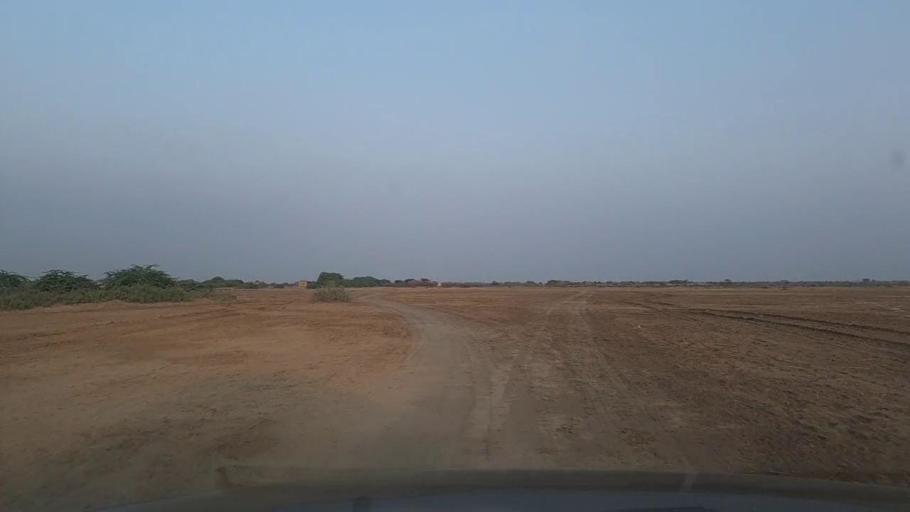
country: PK
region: Sindh
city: Jati
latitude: 24.5294
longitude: 68.4124
